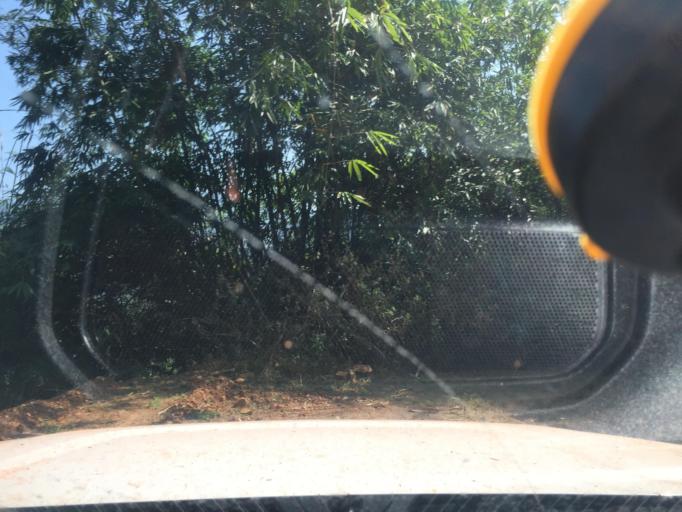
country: LA
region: Phongsali
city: Phongsali
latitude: 21.7047
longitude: 102.3924
